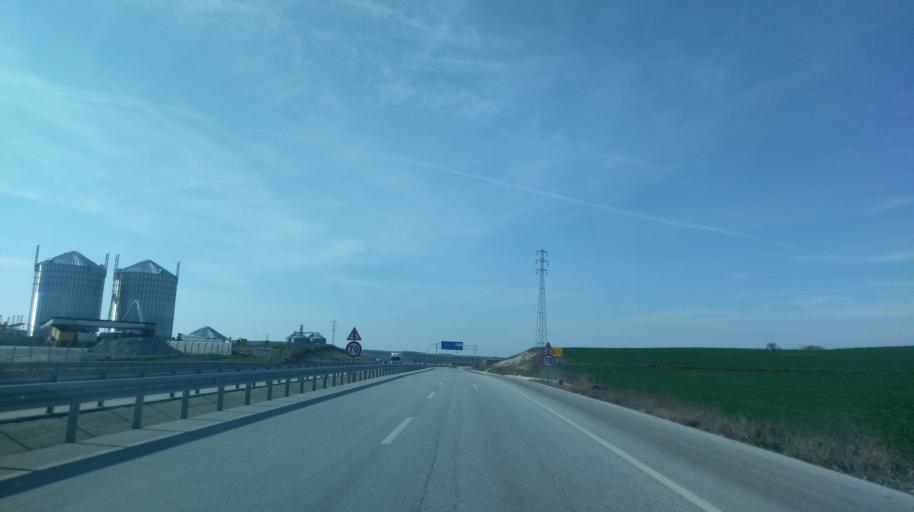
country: TR
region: Edirne
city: Uzun Keupru
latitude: 41.2377
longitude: 26.6897
